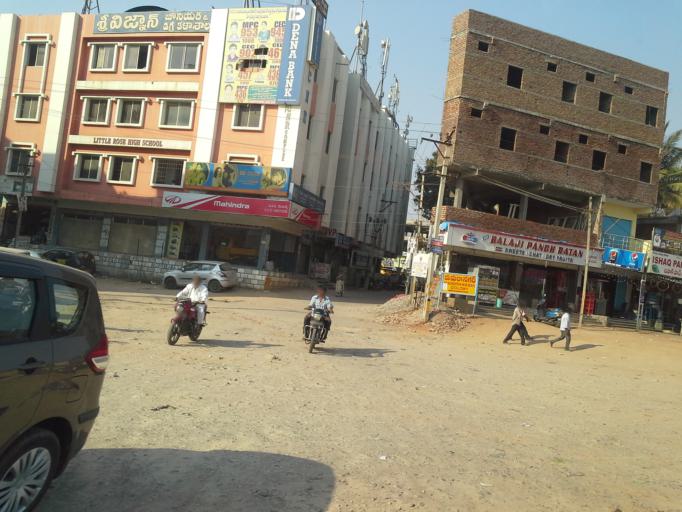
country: IN
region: Telangana
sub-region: Rangareddi
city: Balapur
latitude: 17.2610
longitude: 78.3868
